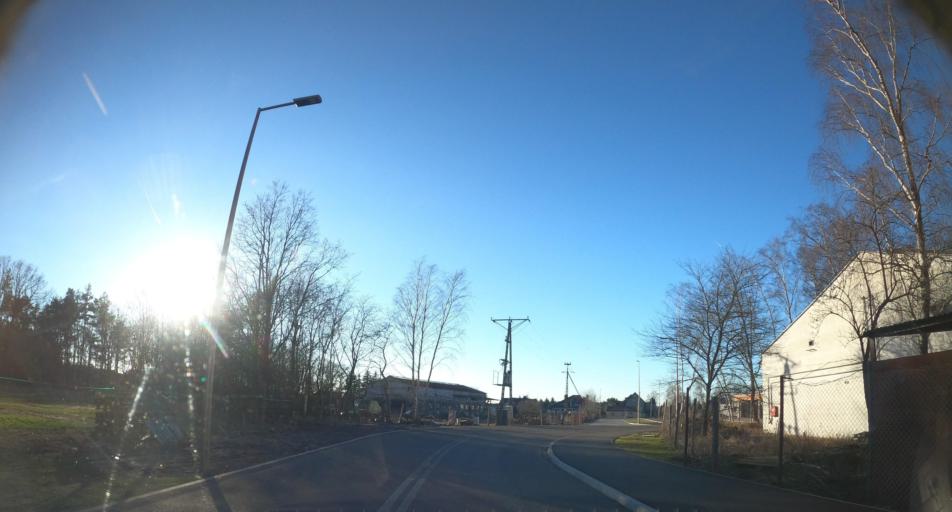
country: PL
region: West Pomeranian Voivodeship
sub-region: Powiat goleniowski
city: Goleniow
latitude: 53.4384
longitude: 14.7402
